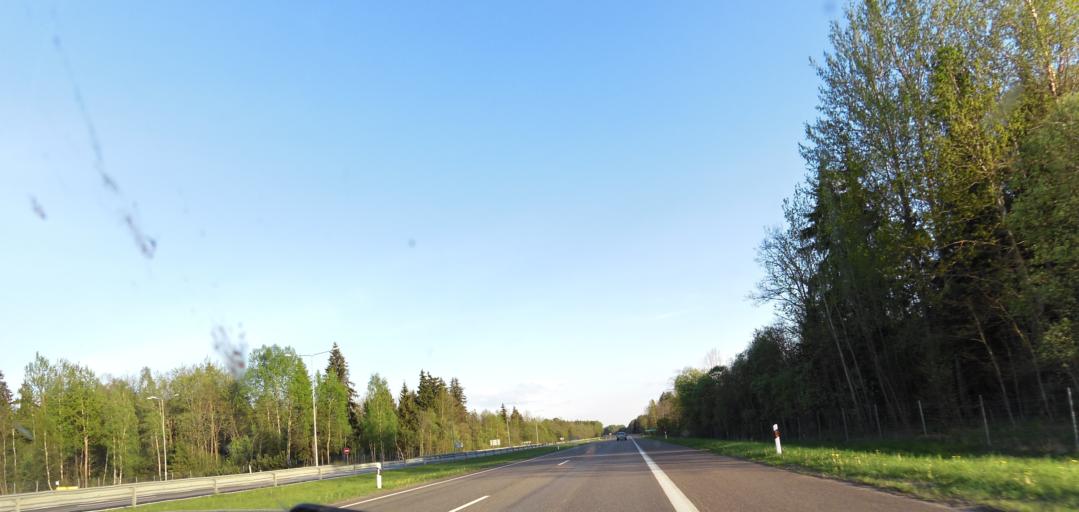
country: LT
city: Sirvintos
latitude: 55.1044
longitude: 24.8529
